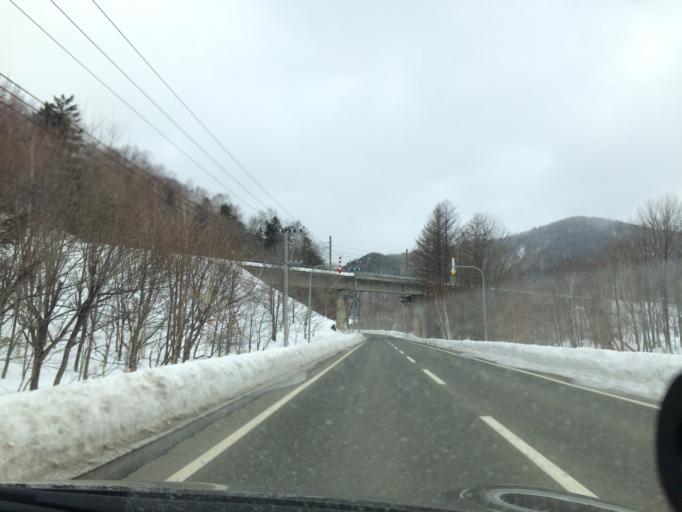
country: JP
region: Hokkaido
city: Shimo-furano
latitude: 43.0610
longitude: 142.5307
